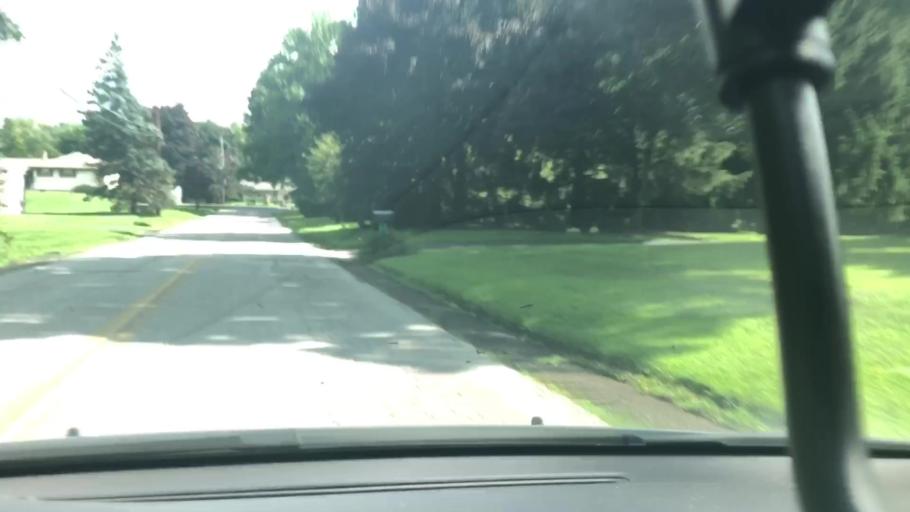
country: US
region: Pennsylvania
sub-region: Chester County
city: Kenilworth
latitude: 40.2036
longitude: -75.6356
